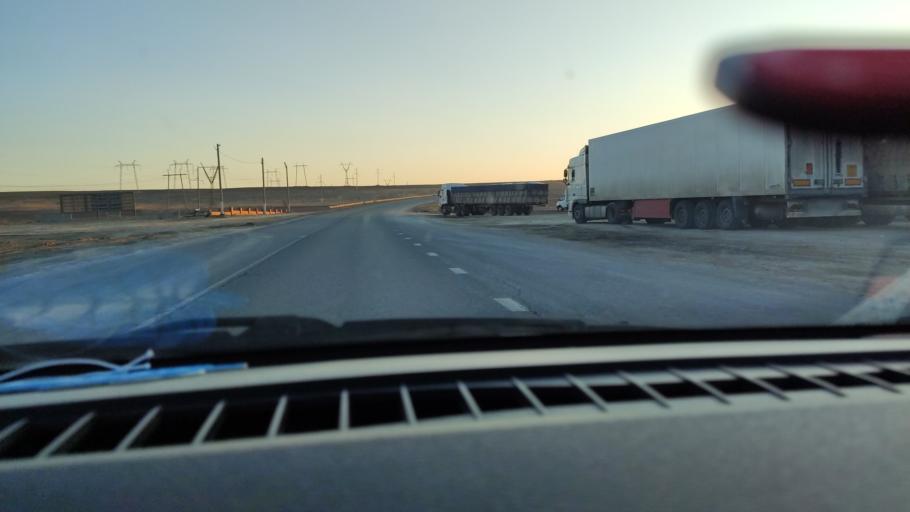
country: RU
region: Saratov
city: Sinodskoye
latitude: 51.9232
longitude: 46.5628
